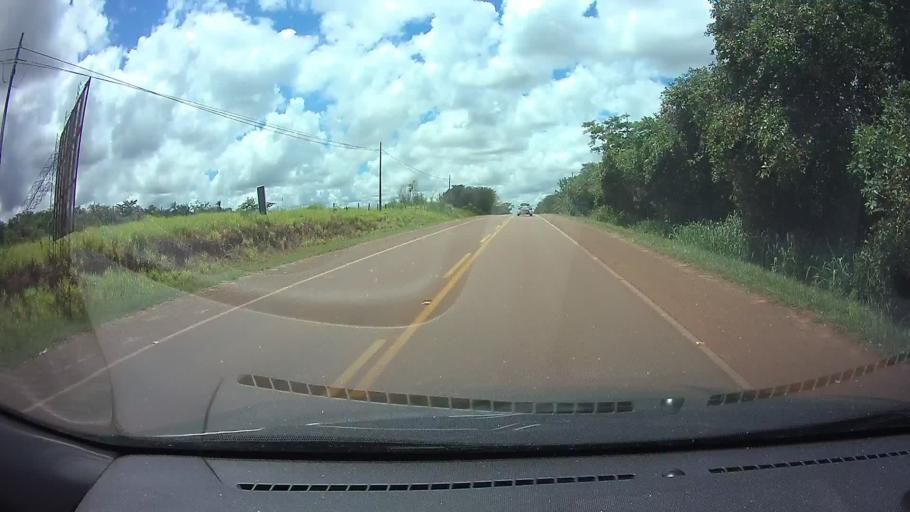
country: PY
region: Paraguari
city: La Colmena
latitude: -25.8914
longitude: -56.8250
